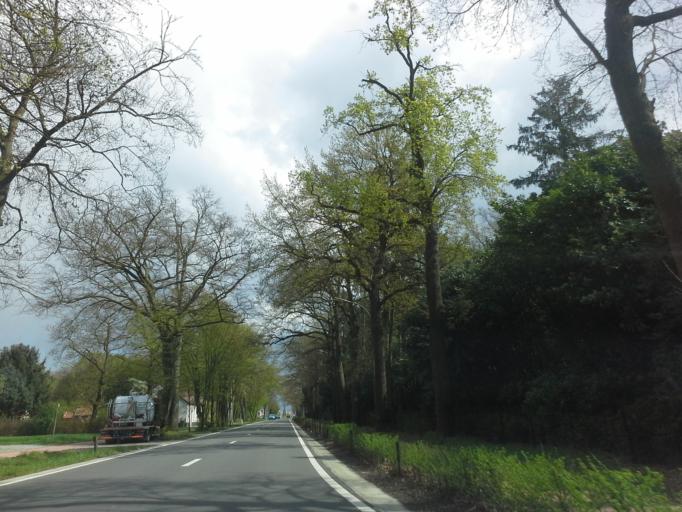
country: BE
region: Flanders
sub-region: Provincie Antwerpen
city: Balen
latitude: 51.2231
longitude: 5.2195
